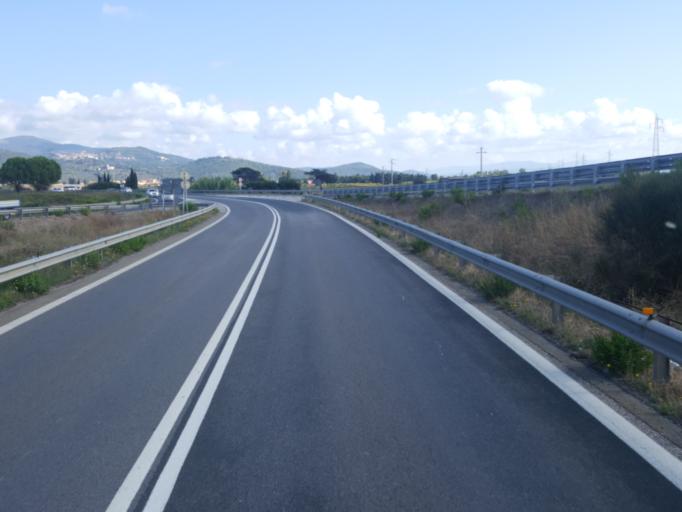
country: IT
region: Tuscany
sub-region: Provincia di Livorno
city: Venturina
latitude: 43.0130
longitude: 10.5994
